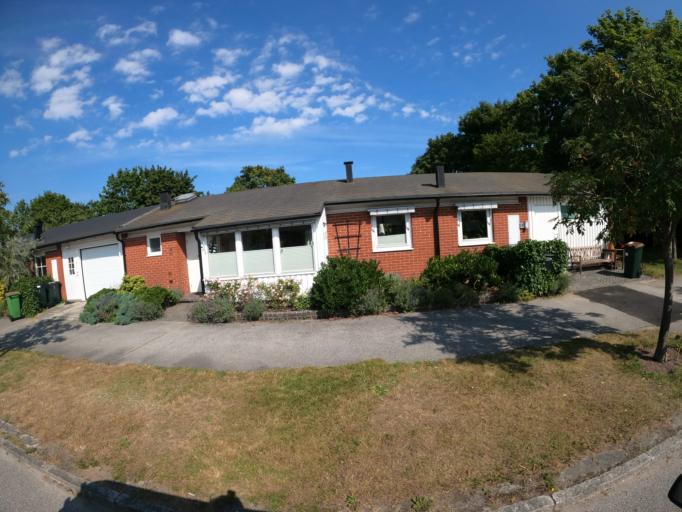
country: SE
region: Skane
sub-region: Lunds Kommun
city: Lund
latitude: 55.7241
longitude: 13.1750
